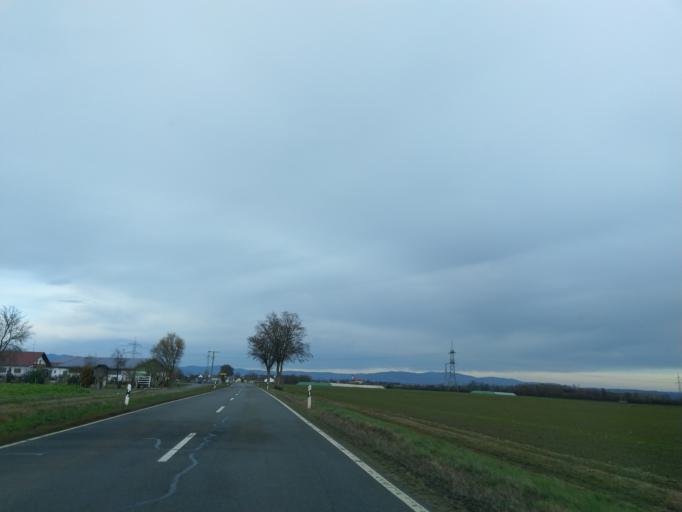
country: DE
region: Bavaria
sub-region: Lower Bavaria
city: Osterhofen
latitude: 48.6678
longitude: 12.9900
